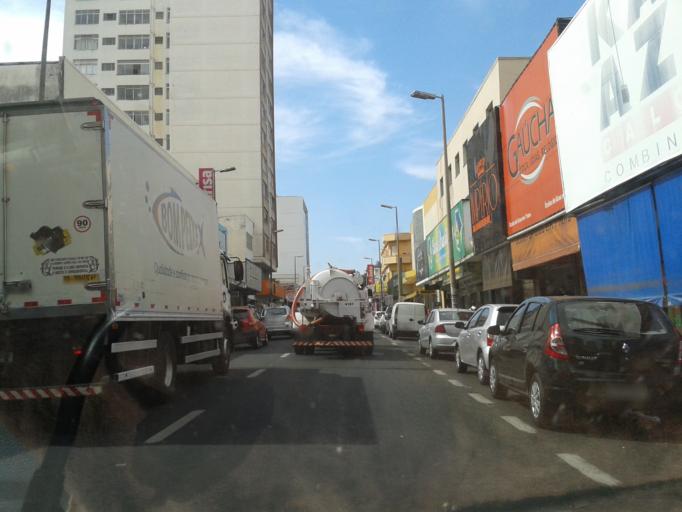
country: BR
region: Minas Gerais
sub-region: Uberlandia
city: Uberlandia
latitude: -18.9184
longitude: -48.2778
